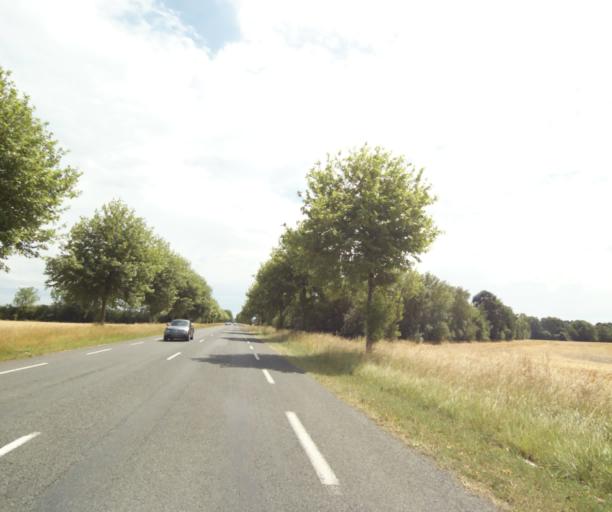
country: FR
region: Ile-de-France
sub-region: Departement de Seine-et-Marne
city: Chailly-en-Biere
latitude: 48.4830
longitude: 2.5932
